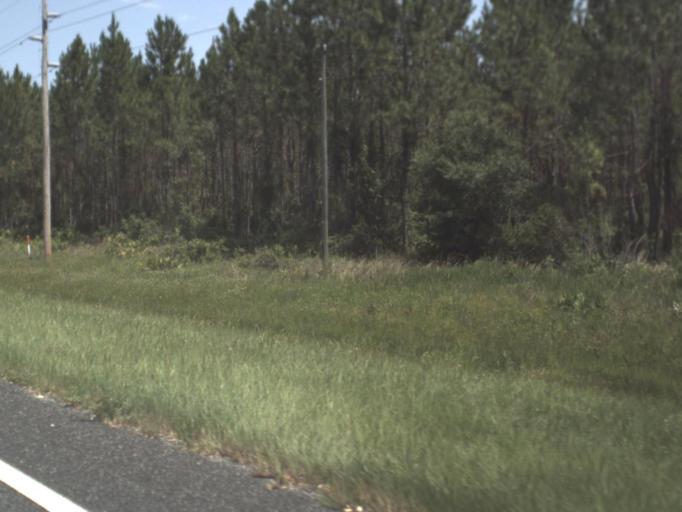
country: US
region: Florida
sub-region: Taylor County
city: Steinhatchee
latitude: 29.7080
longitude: -83.2927
